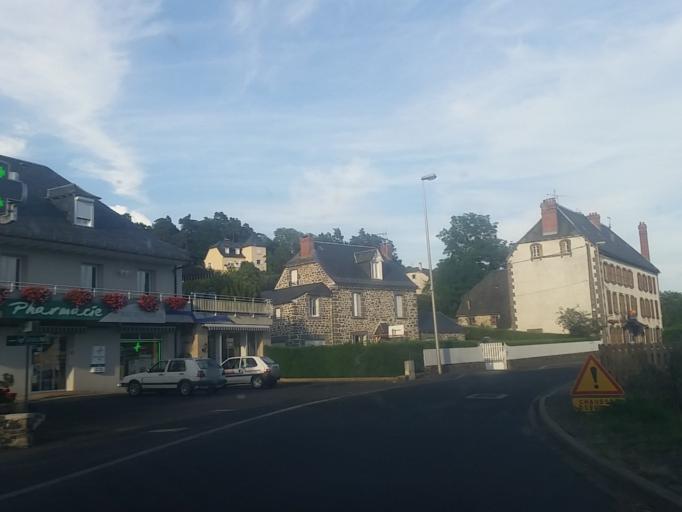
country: FR
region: Auvergne
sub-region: Departement du Cantal
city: Neuveglise
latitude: 44.9311
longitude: 2.9848
